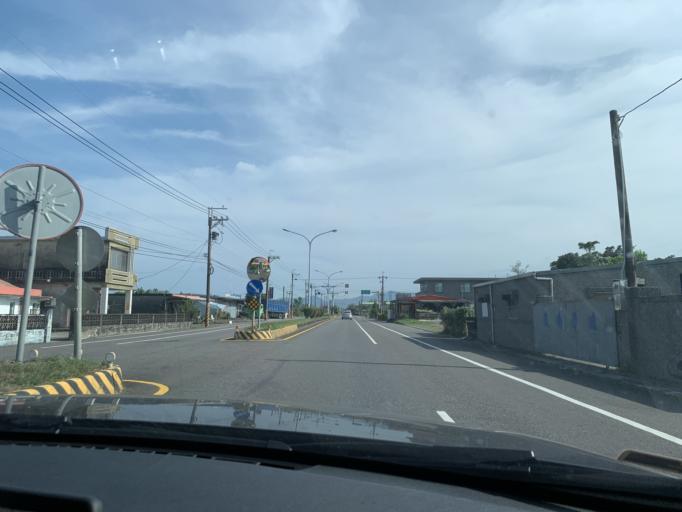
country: TW
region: Taiwan
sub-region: Yilan
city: Yilan
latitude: 24.7445
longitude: 121.8164
